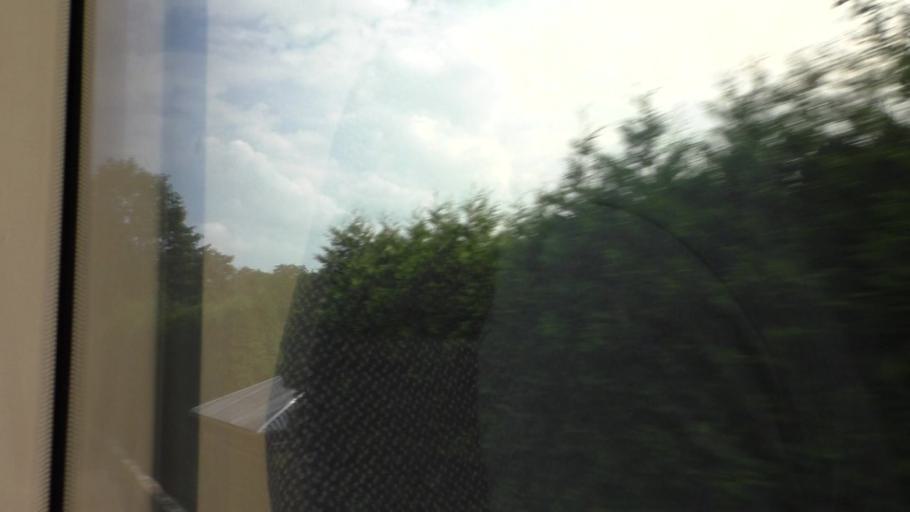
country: DE
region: Brandenburg
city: Konigs Wusterhausen
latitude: 52.2992
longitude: 13.6728
